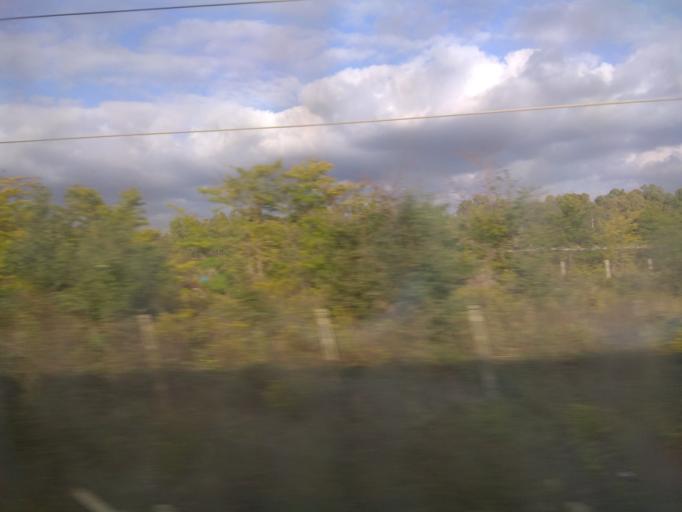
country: IT
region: Latium
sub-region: Citta metropolitana di Roma Capitale
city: Maccarese
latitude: 41.9077
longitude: 12.2087
